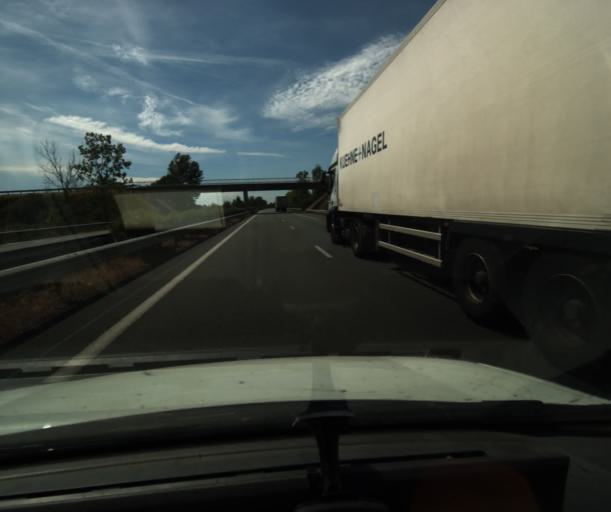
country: FR
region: Midi-Pyrenees
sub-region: Departement du Tarn-et-Garonne
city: Saint-Porquier
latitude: 44.0166
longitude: 1.1915
